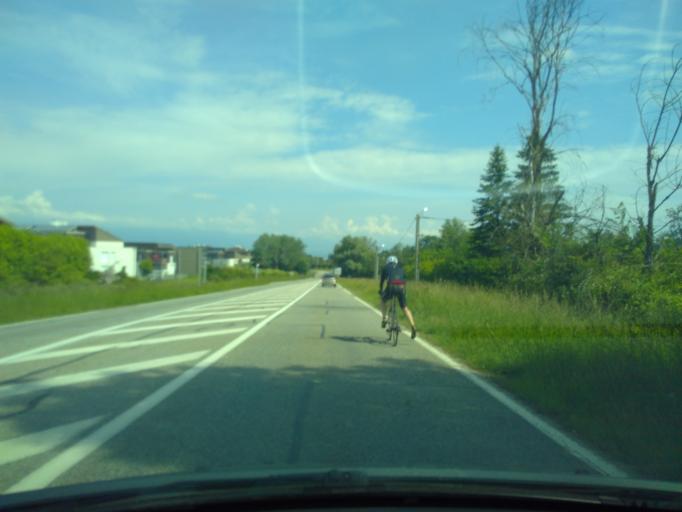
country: FR
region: Rhone-Alpes
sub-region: Departement de la Haute-Savoie
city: Beaumont
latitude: 46.0946
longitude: 6.1041
